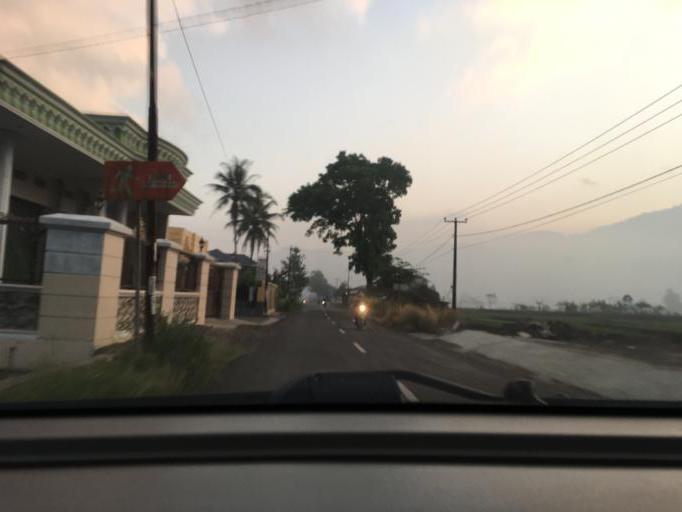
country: ID
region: West Java
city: Padamulya
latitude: -7.2027
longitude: 108.1995
